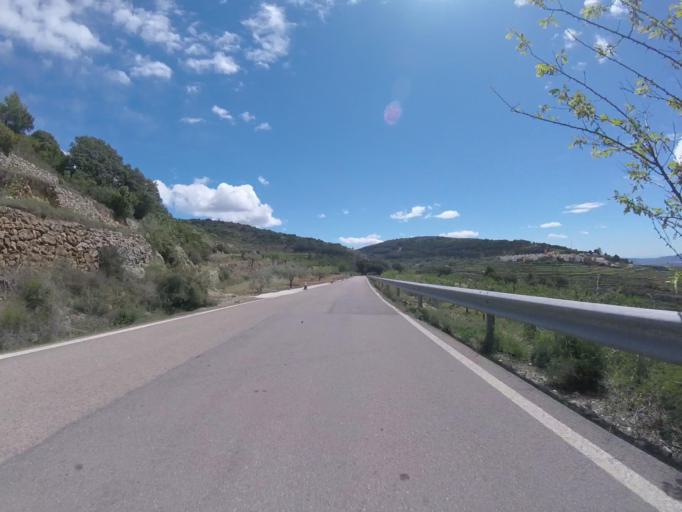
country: ES
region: Valencia
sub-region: Provincia de Castello
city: Sierra-Engarceran
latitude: 40.2753
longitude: -0.0259
